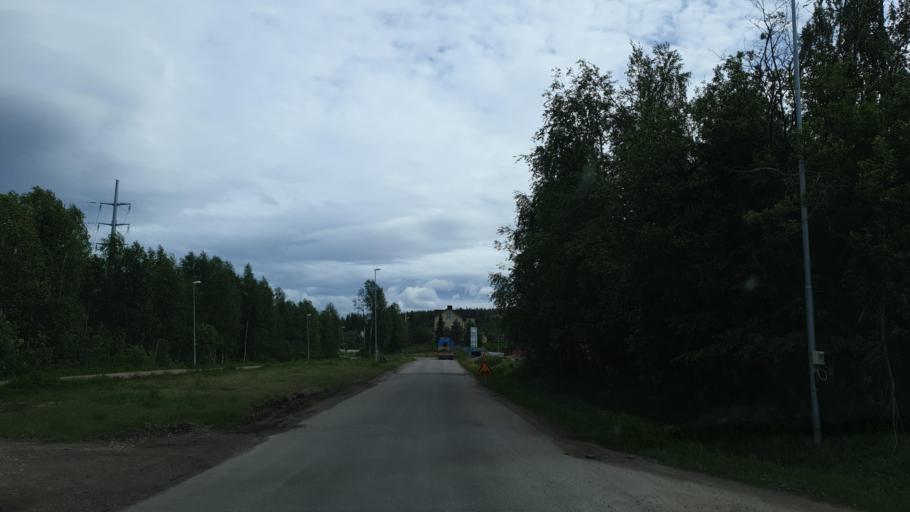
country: SE
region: Norrbotten
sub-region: Gallivare Kommun
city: Gaellivare
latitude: 67.1295
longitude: 20.6477
